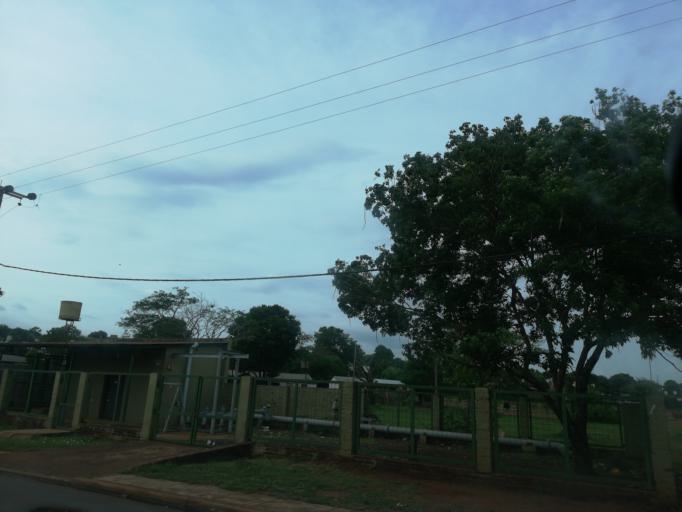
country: AR
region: Misiones
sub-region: Departamento de Capital
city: Posadas
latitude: -27.4314
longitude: -55.9100
